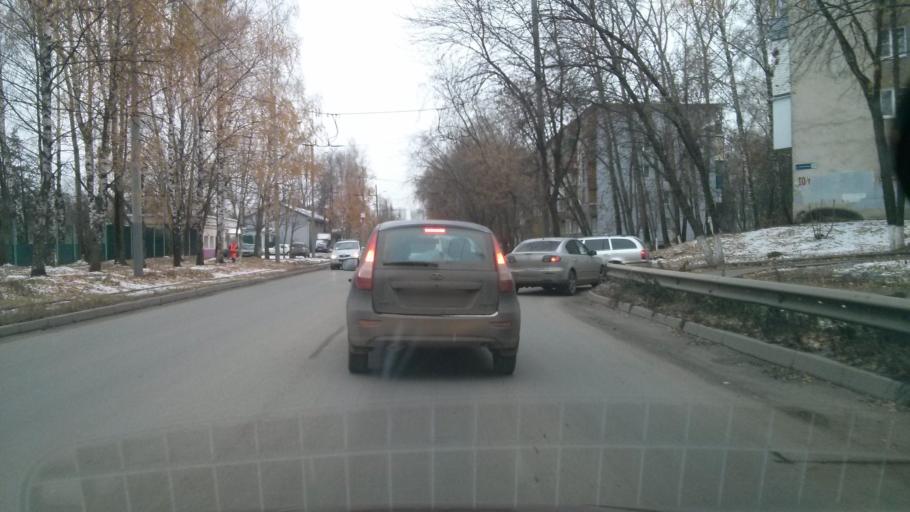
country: RU
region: Nizjnij Novgorod
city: Nizhniy Novgorod
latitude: 56.3006
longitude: 44.0480
